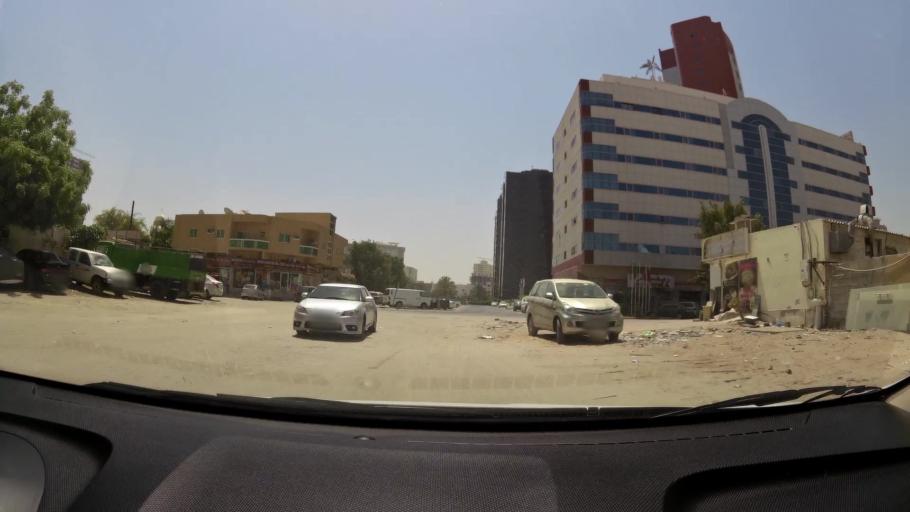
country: AE
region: Ajman
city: Ajman
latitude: 25.3907
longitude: 55.4603
